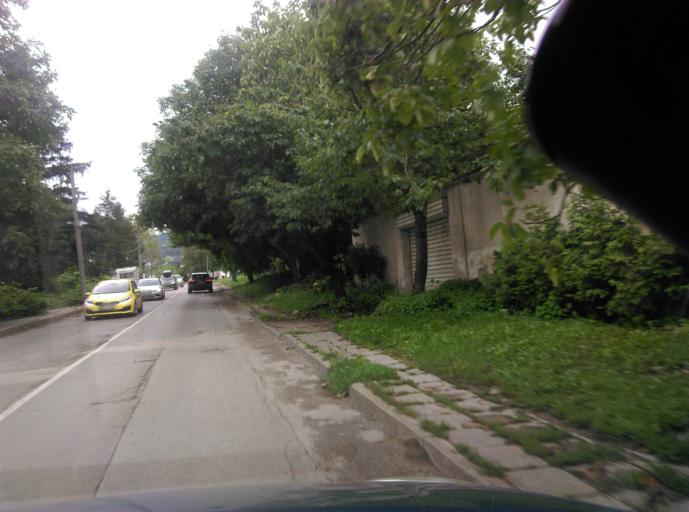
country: BG
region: Sofia-Capital
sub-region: Stolichna Obshtina
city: Sofia
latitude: 42.6276
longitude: 23.3170
